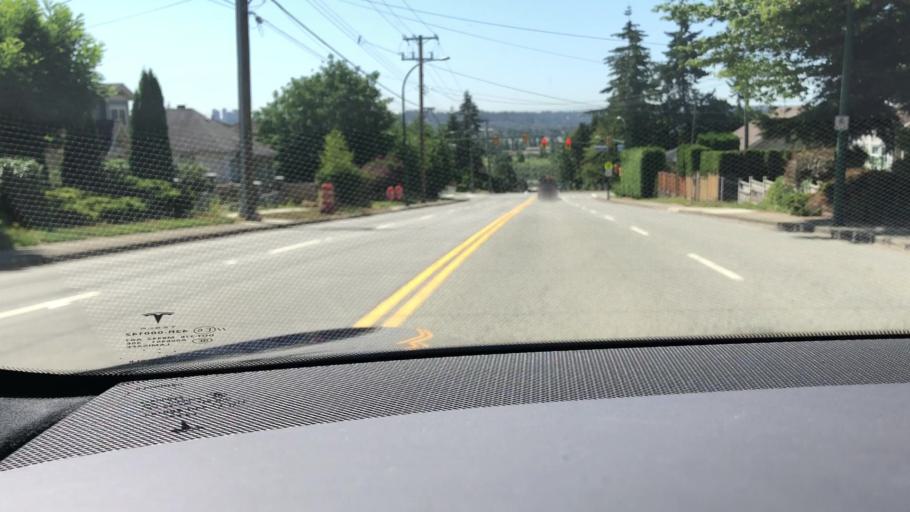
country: CA
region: British Columbia
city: Port Moody
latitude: 49.2407
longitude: -122.8730
